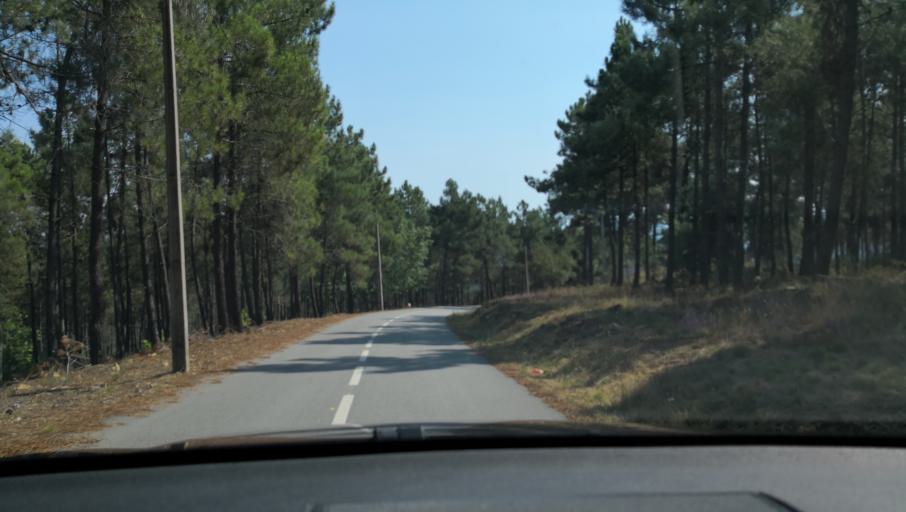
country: PT
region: Vila Real
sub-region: Sabrosa
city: Sabrosa
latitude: 41.2749
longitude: -7.6189
